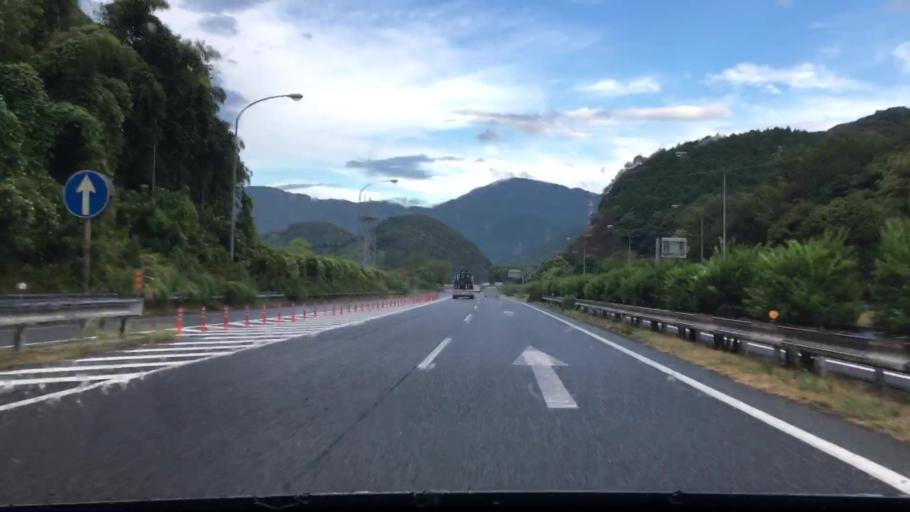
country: JP
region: Fukuoka
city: Kitakyushu
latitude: 33.8031
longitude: 130.8546
